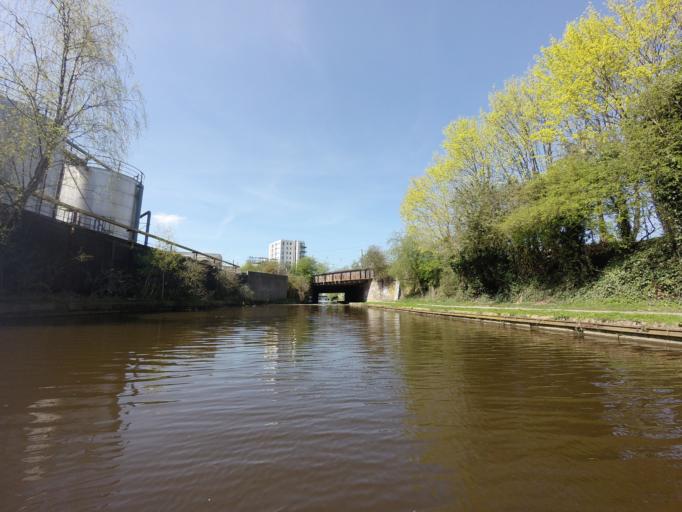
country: GB
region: England
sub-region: Greater London
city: Hayes
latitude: 51.5023
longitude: -0.4144
